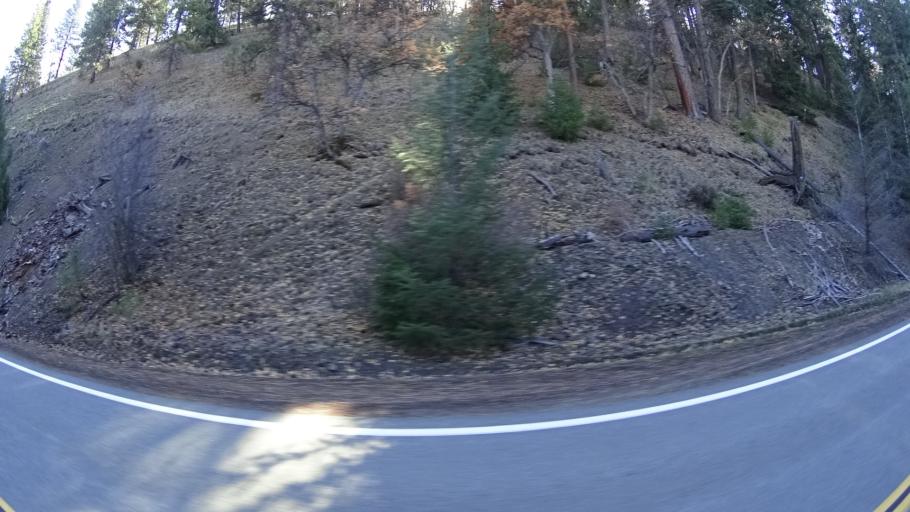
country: US
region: California
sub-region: Siskiyou County
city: Weed
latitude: 41.4632
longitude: -122.6178
